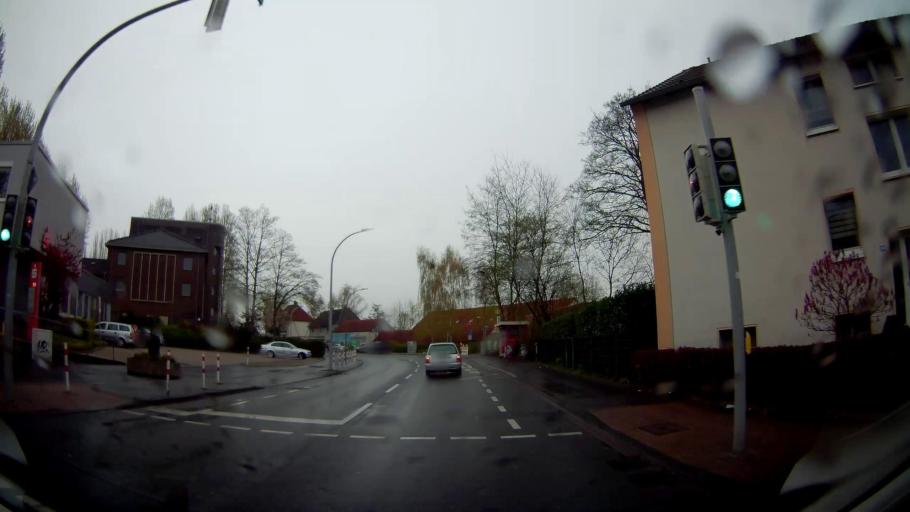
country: DE
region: North Rhine-Westphalia
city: Castrop-Rauxel
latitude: 51.5225
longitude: 7.3741
